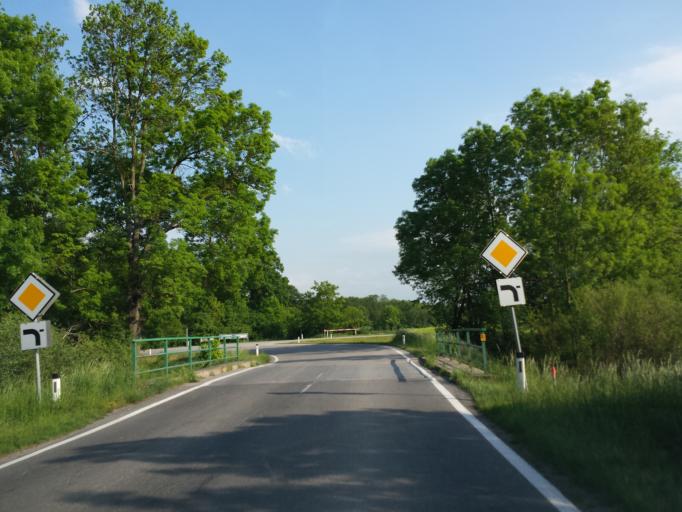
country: AT
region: Lower Austria
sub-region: Politischer Bezirk Ganserndorf
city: Marchegg
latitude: 48.2778
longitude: 16.8956
